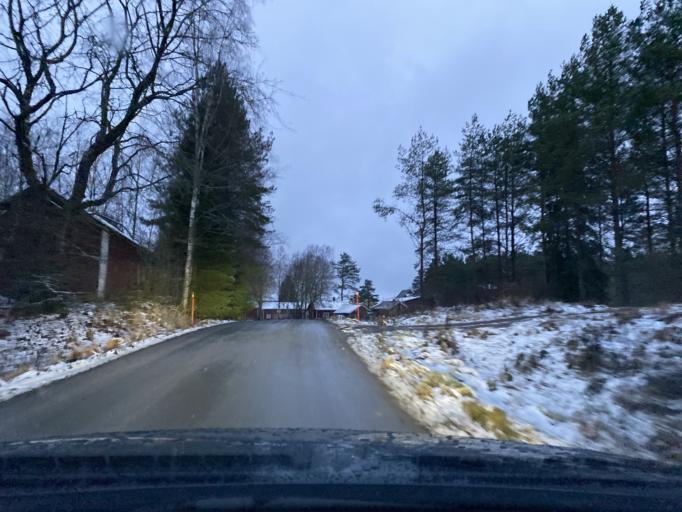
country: FI
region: Pirkanmaa
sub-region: Lounais-Pirkanmaa
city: Punkalaidun
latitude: 61.1409
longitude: 22.9649
